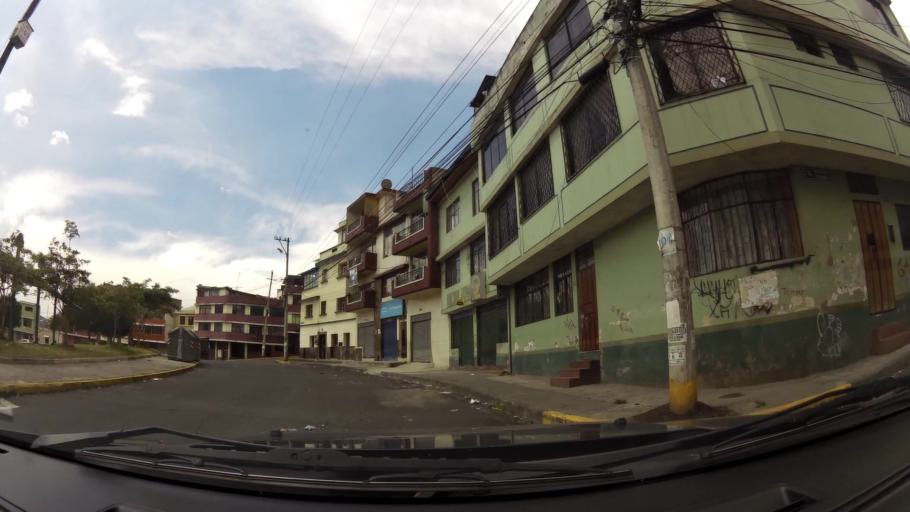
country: EC
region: Pichincha
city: Quito
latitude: -0.2580
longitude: -78.5163
